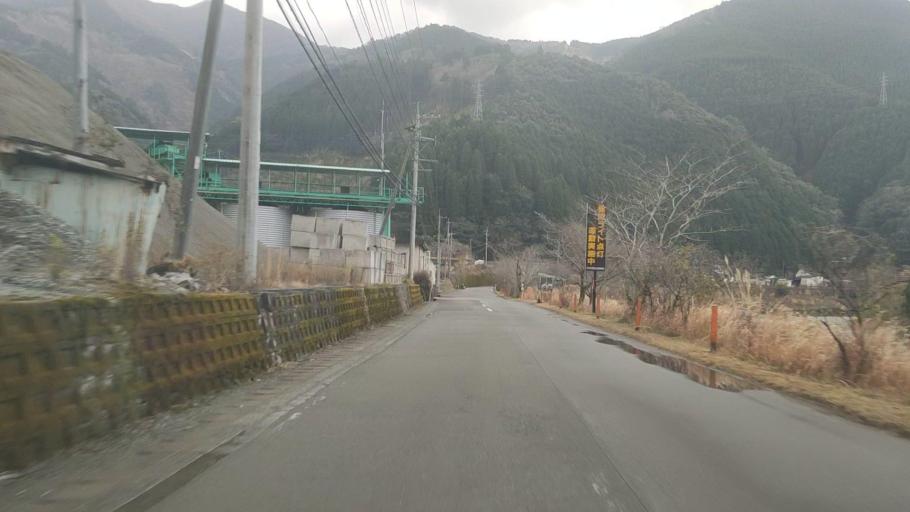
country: JP
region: Kumamoto
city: Hitoyoshi
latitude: 32.4360
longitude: 130.8581
